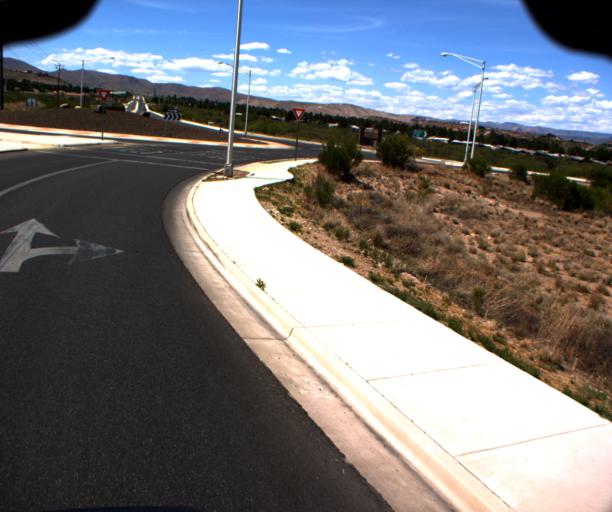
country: US
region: Arizona
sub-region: Yavapai County
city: Clarkdale
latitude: 34.7467
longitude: -112.0446
